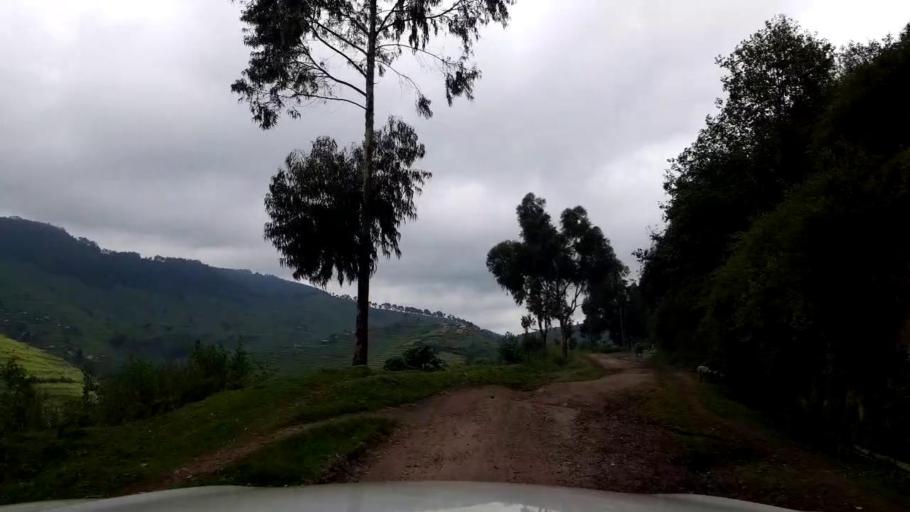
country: RW
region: Western Province
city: Gisenyi
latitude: -1.6599
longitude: 29.4181
